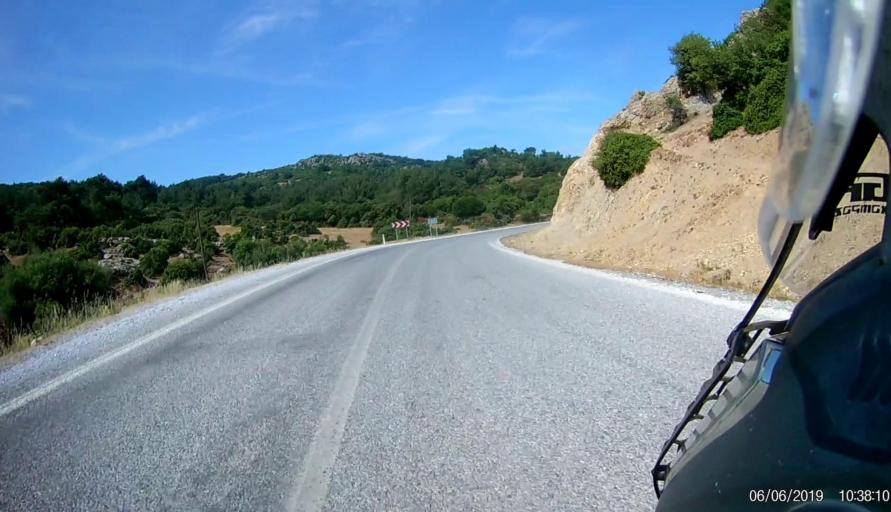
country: TR
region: Canakkale
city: Ayvacik
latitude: 39.5222
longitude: 26.4621
